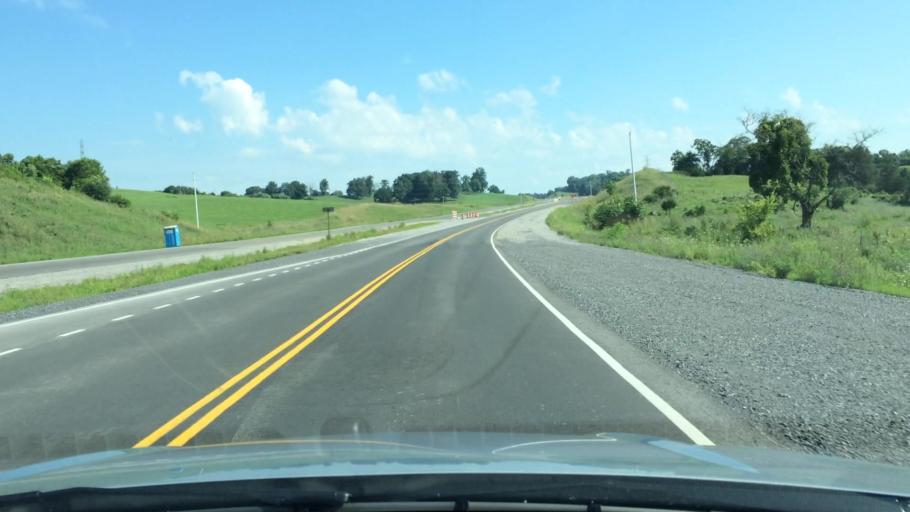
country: US
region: Tennessee
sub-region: Jefferson County
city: White Pine
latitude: 36.1434
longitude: -83.3434
